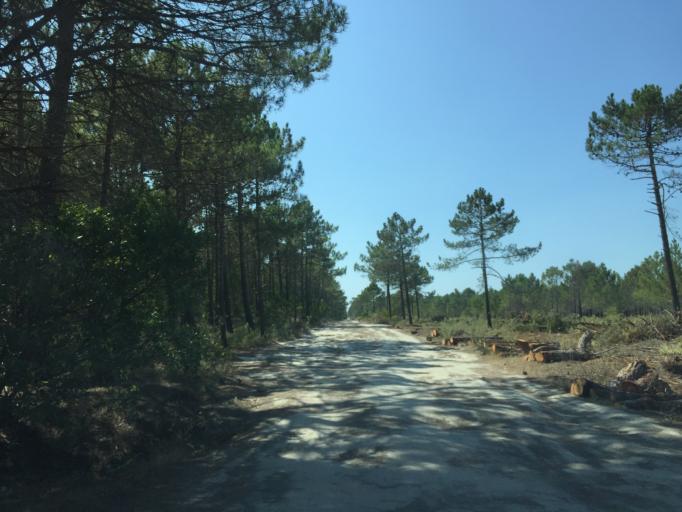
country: PT
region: Coimbra
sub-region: Figueira da Foz
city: Tavarede
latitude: 40.2579
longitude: -8.8406
